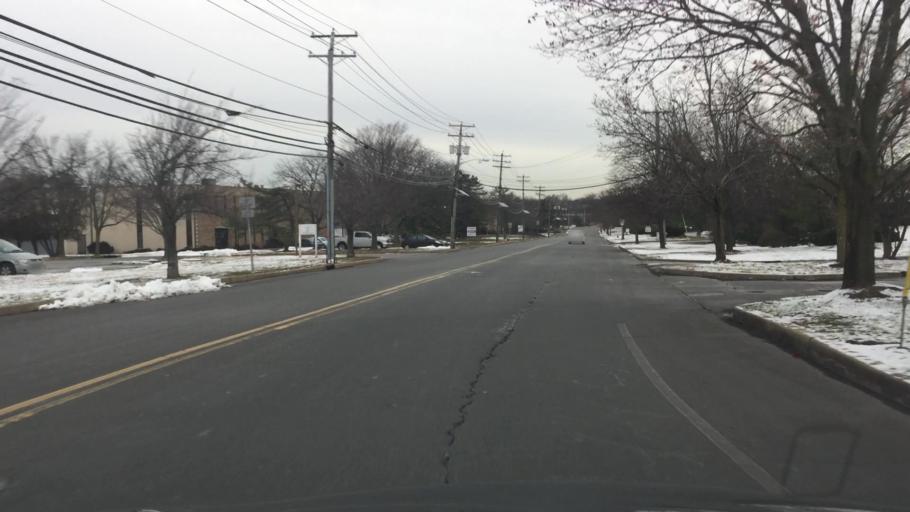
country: US
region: New Jersey
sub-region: Middlesex County
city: Edison
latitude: 40.5279
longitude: -74.4323
